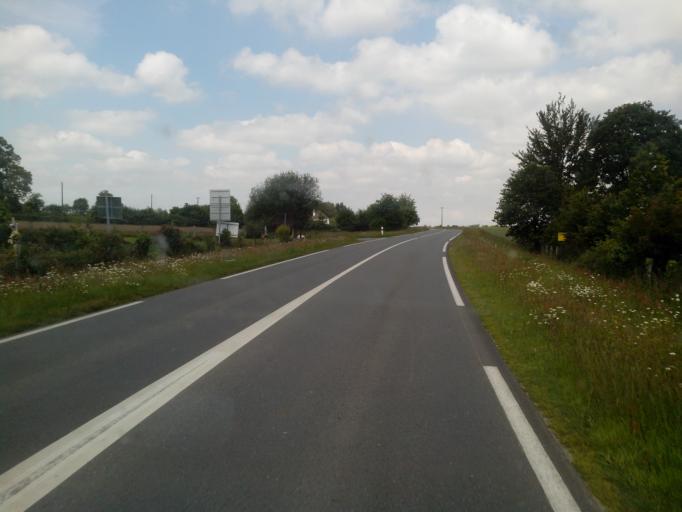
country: FR
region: Brittany
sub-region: Departement d'Ille-et-Vilaine
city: Lecousse
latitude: 48.3738
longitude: -1.2468
